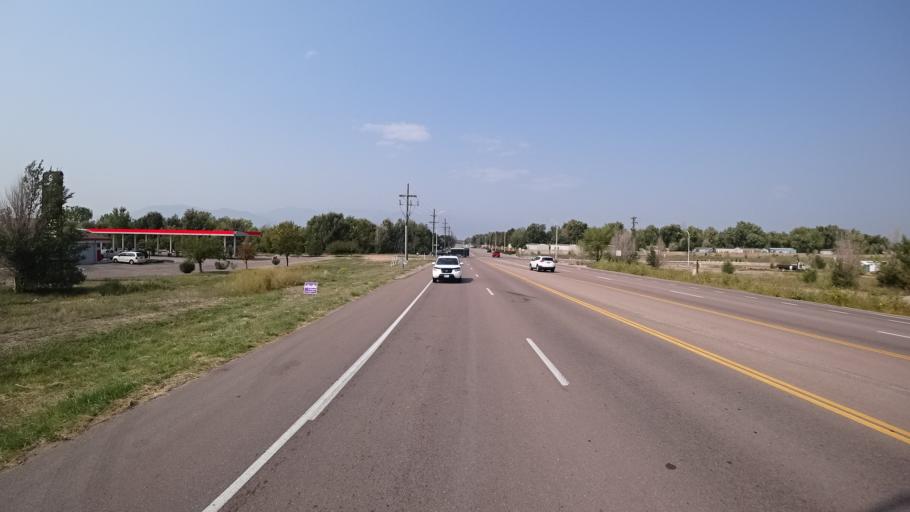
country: US
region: Colorado
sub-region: El Paso County
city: Cimarron Hills
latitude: 38.8248
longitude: -104.7281
